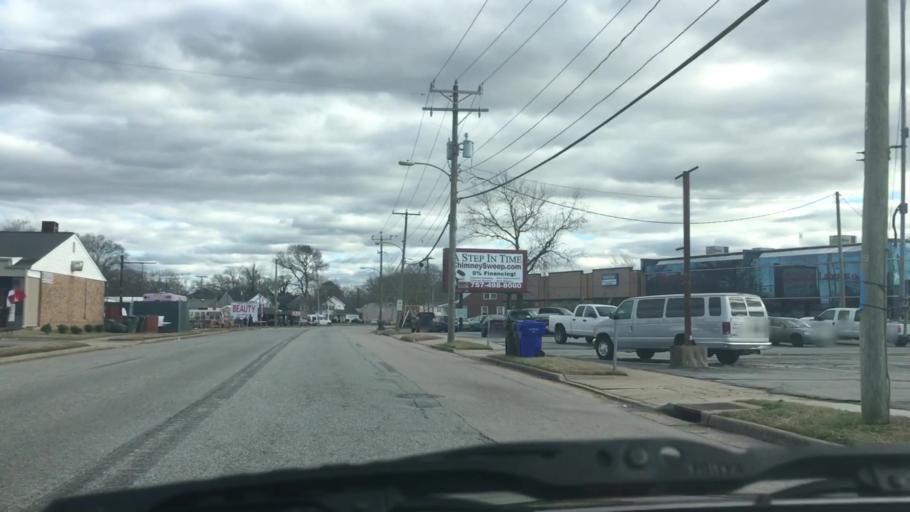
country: US
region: Virginia
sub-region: City of Norfolk
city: Norfolk
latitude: 36.9138
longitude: -76.2488
